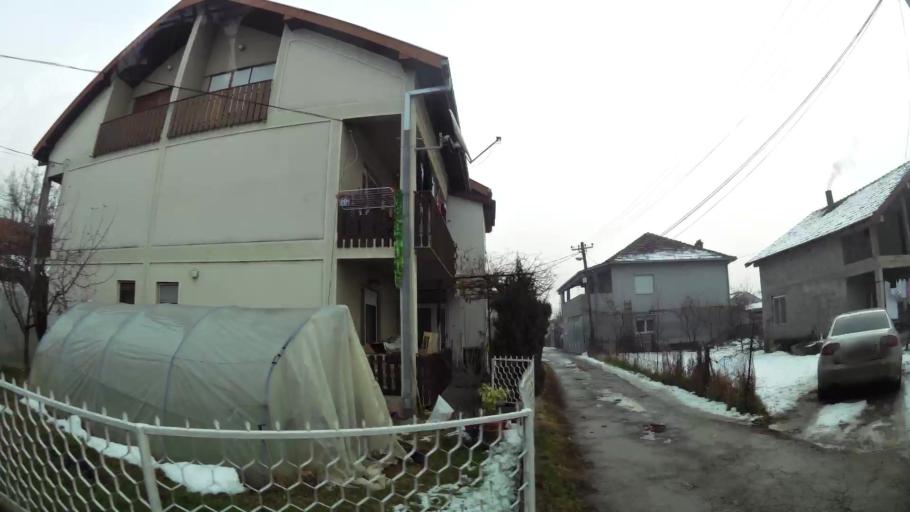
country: MK
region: Ilinden
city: Jurumleri
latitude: 41.9689
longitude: 21.5606
